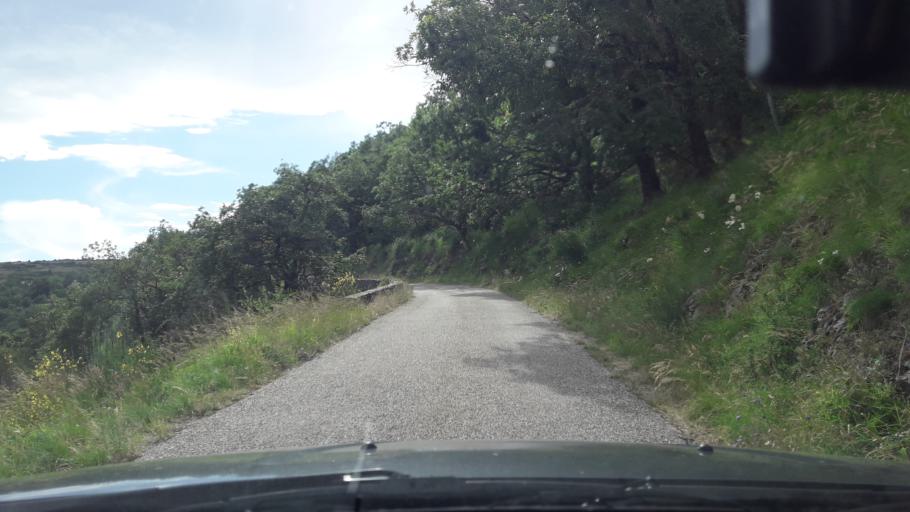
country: FR
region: Rhone-Alpes
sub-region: Departement de l'Ardeche
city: Saint-Priest
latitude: 44.6807
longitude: 4.5813
